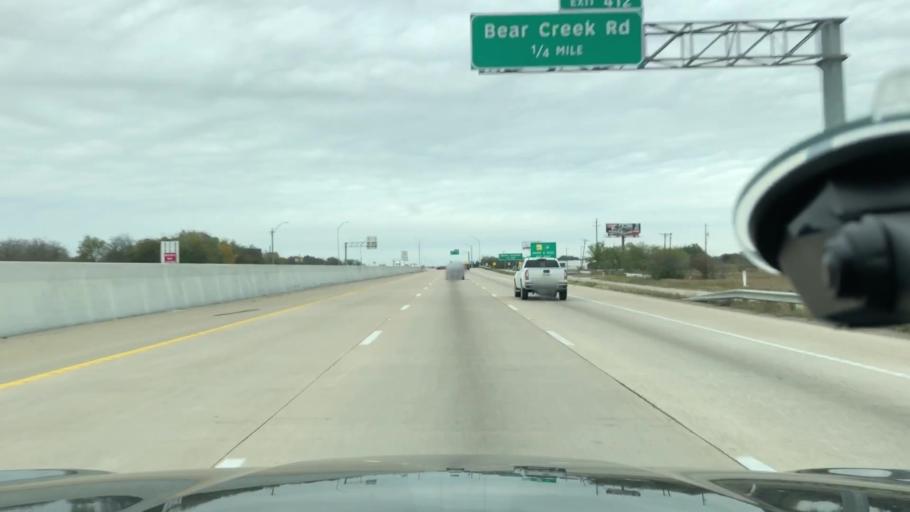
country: US
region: Texas
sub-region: Ellis County
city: Red Oak
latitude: 32.5437
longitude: -96.8221
